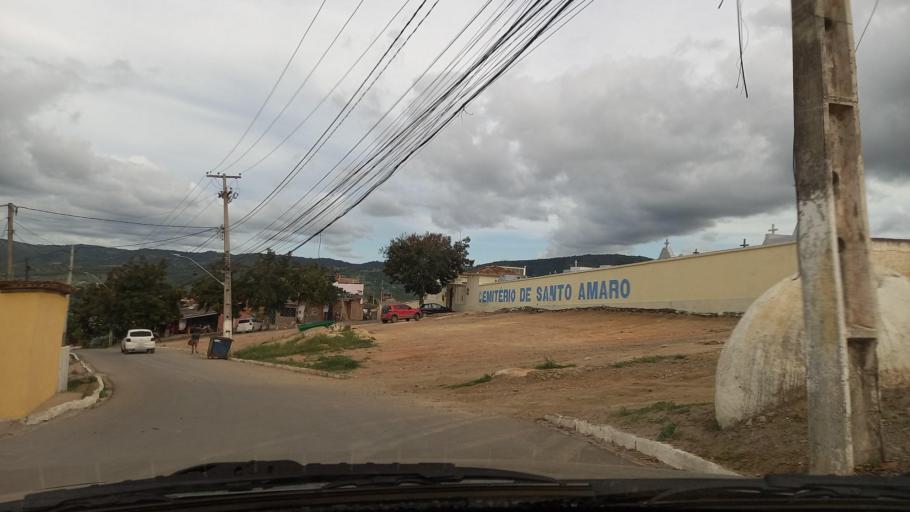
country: BR
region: Pernambuco
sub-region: Gravata
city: Gravata
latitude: -8.2116
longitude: -35.5743
